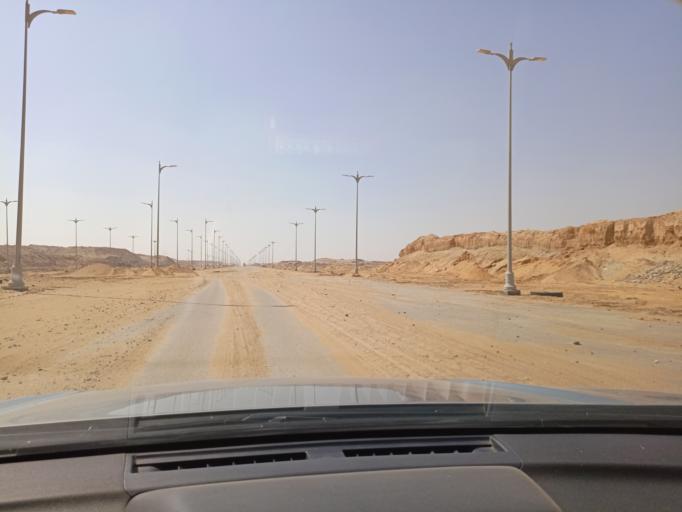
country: EG
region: Muhafazat al Qalyubiyah
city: Al Khankah
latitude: 30.0083
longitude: 31.6245
